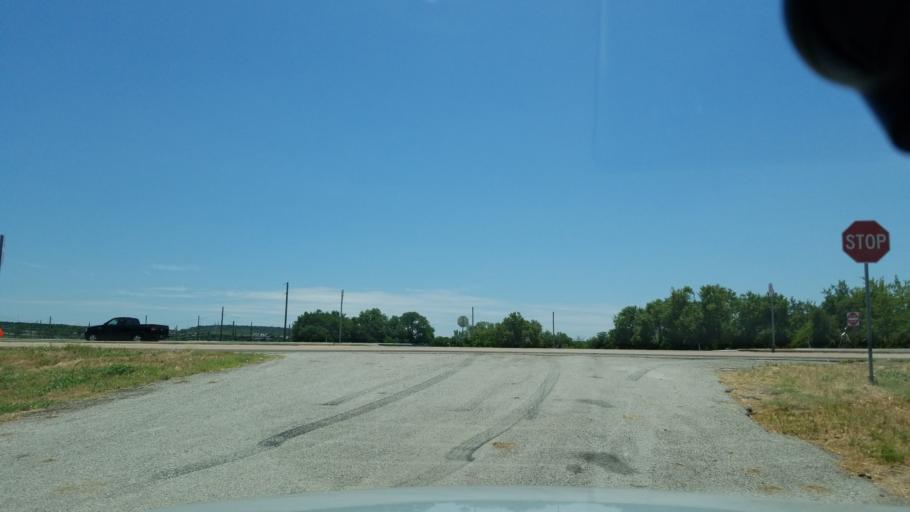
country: US
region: Texas
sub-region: Dallas County
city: Cockrell Hill
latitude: 32.7499
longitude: -96.9356
